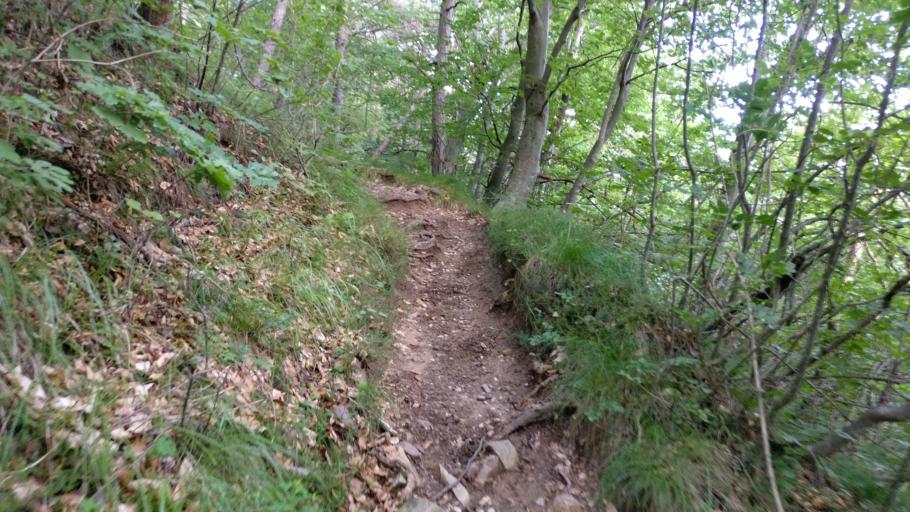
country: IT
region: Trentino-Alto Adige
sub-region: Bolzano
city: San Paolo
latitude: 46.4746
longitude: 11.2325
